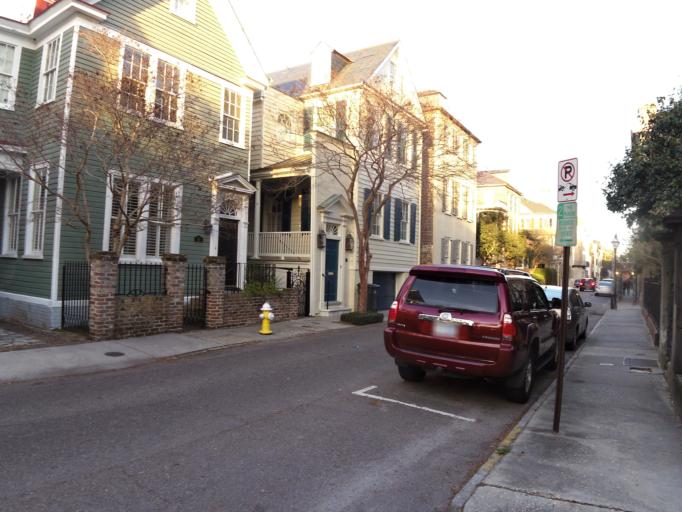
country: US
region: South Carolina
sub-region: Charleston County
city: Charleston
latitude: 32.7745
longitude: -79.9318
